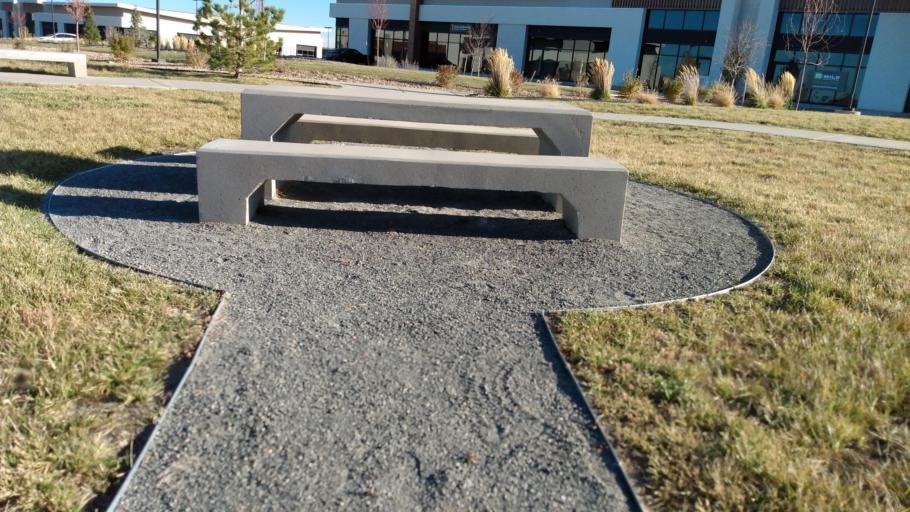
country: US
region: Colorado
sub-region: Boulder County
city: Louisville
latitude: 39.9698
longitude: -105.1225
